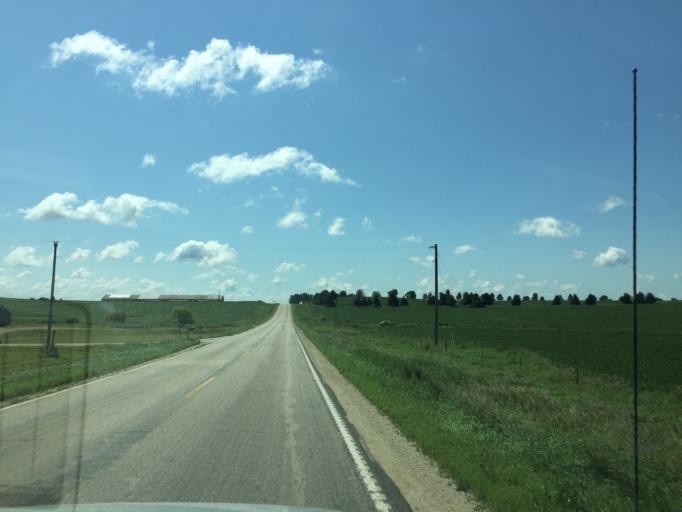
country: US
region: Minnesota
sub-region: Olmsted County
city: Byron
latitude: 44.0180
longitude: -92.6083
